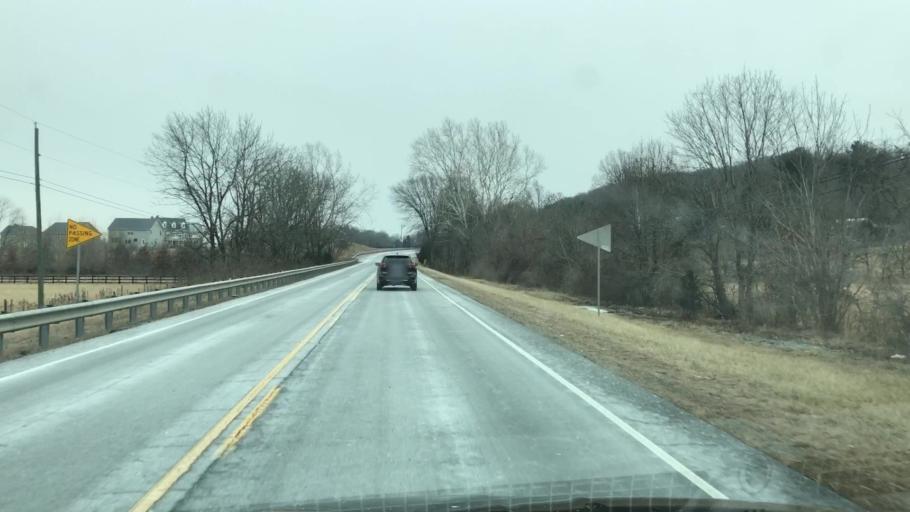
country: US
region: Virginia
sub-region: Loudoun County
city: Leesburg
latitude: 39.0719
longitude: -77.6087
